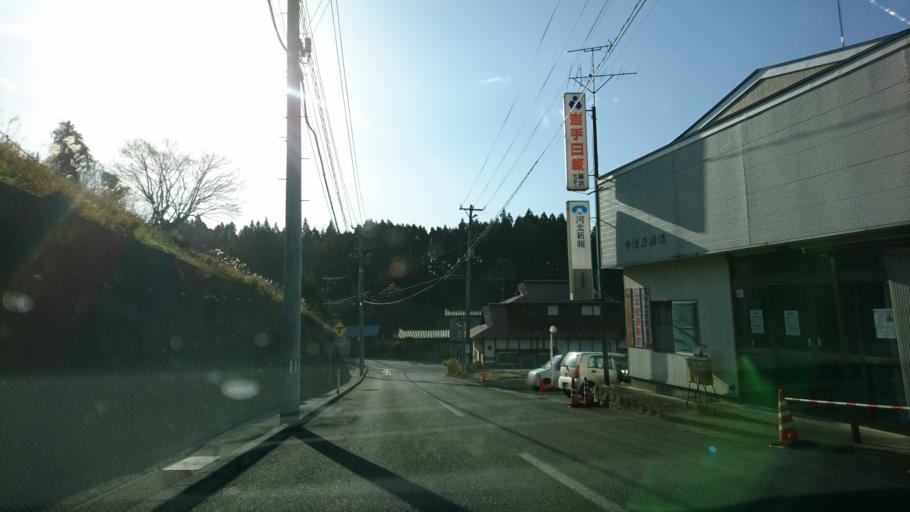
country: JP
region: Iwate
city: Ichinoseki
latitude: 38.8601
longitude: 141.3419
